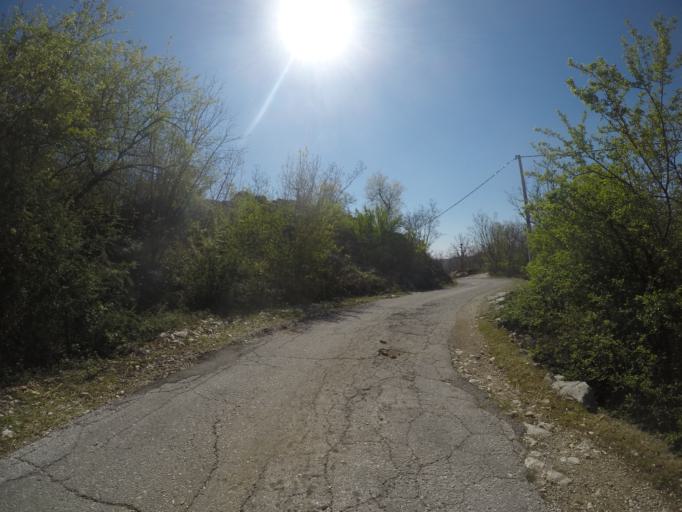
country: ME
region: Danilovgrad
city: Danilovgrad
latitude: 42.5285
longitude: 19.0361
